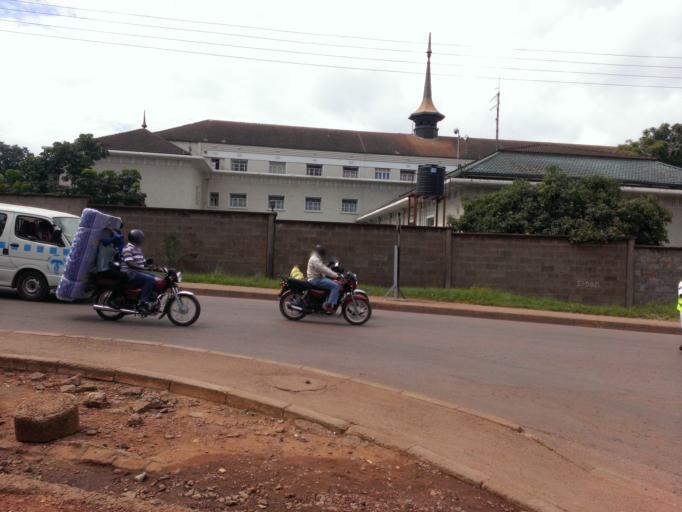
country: UG
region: Central Region
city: Kampala Central Division
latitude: 0.3104
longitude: 32.5578
